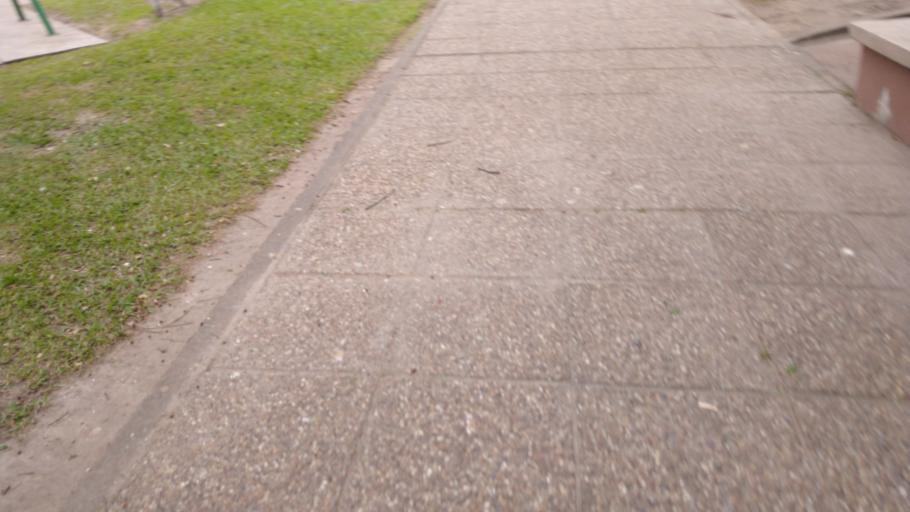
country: AR
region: Entre Rios
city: Villa del Rosario
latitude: -30.7956
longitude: -57.9142
